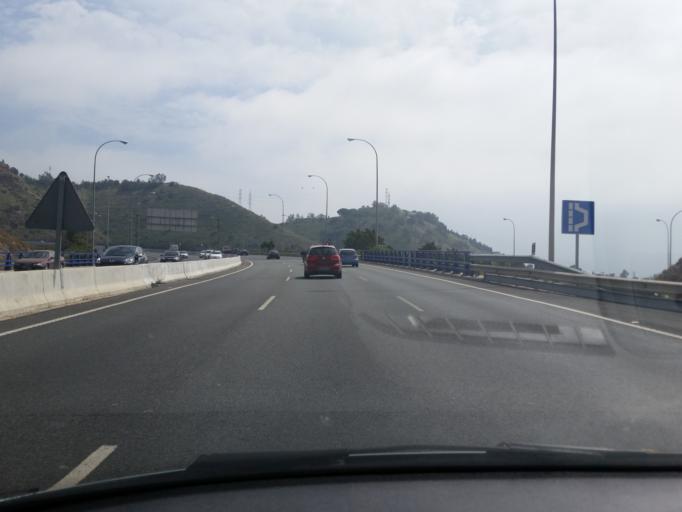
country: ES
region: Andalusia
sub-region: Provincia de Malaga
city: Malaga
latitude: 36.7390
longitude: -4.3953
